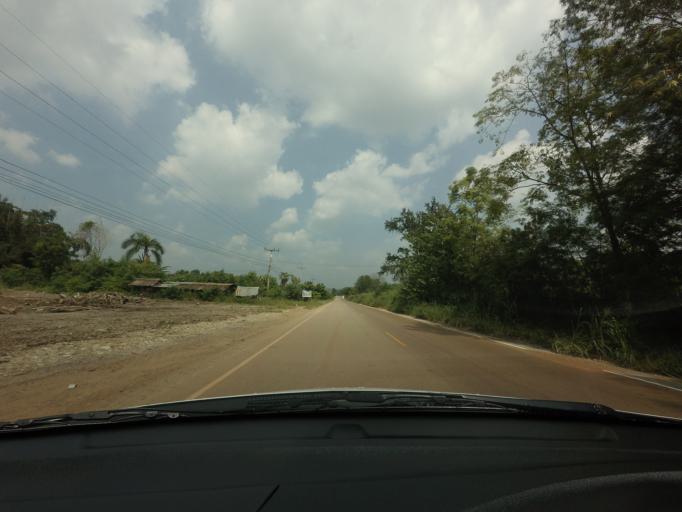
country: TH
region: Nakhon Ratchasima
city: Pak Chong
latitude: 14.5586
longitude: 101.5726
